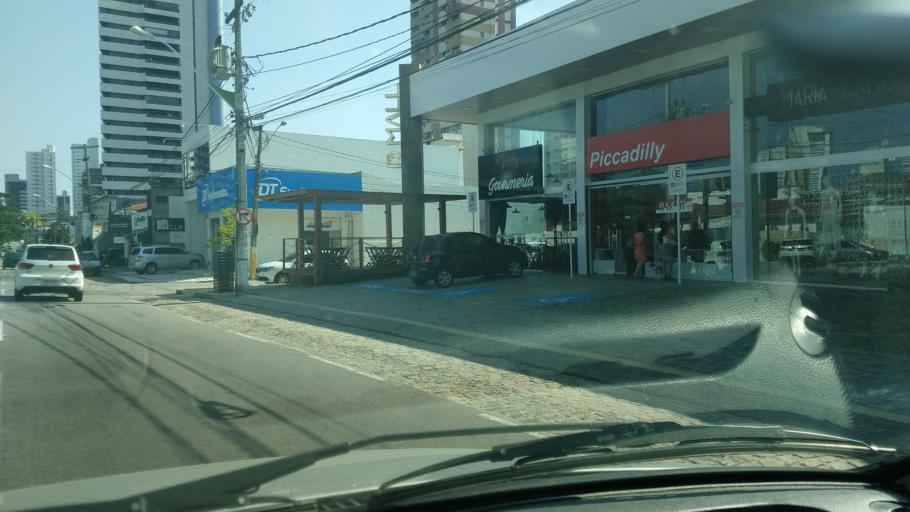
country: BR
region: Rio Grande do Norte
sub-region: Natal
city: Natal
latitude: -5.7955
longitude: -35.2000
